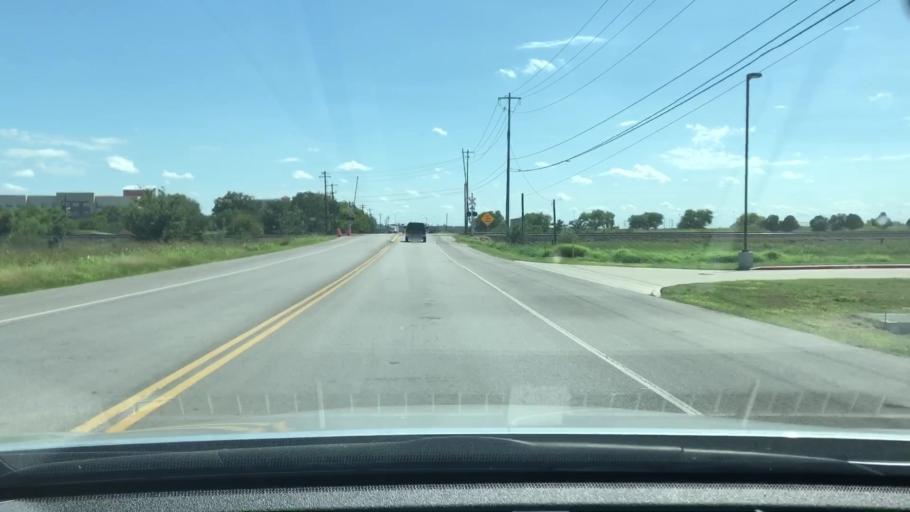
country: US
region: Texas
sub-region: Hays County
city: San Marcos
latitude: 29.8442
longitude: -97.9775
